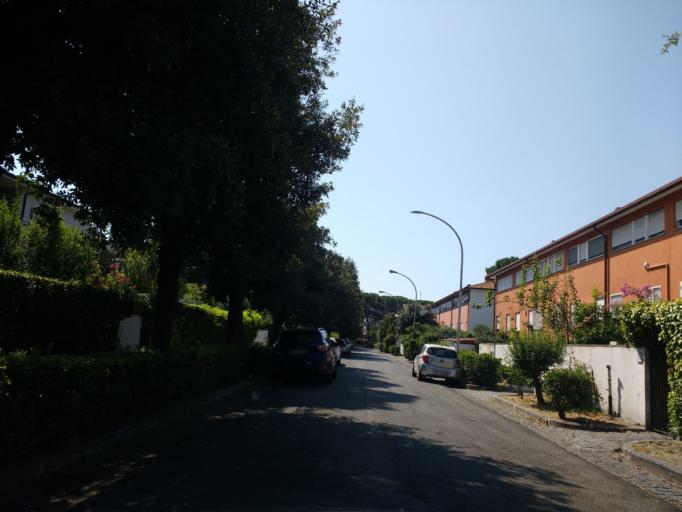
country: IT
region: Latium
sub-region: Citta metropolitana di Roma Capitale
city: Acilia-Castel Fusano-Ostia Antica
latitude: 41.7555
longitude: 12.3561
